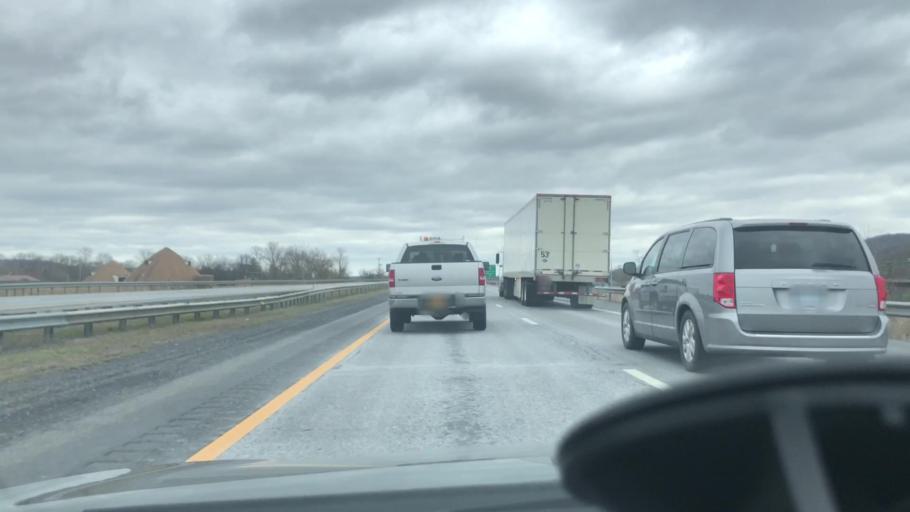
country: US
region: New York
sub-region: Herkimer County
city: Mohawk
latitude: 43.0173
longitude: -75.0003
